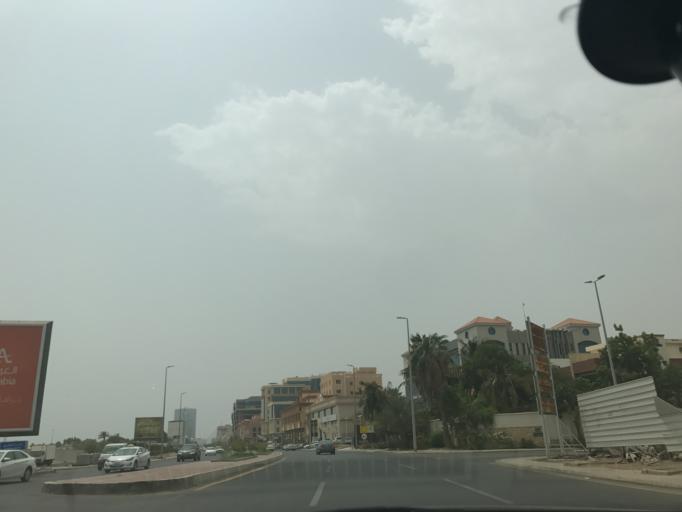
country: SA
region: Makkah
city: Jeddah
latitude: 21.5587
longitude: 39.1458
